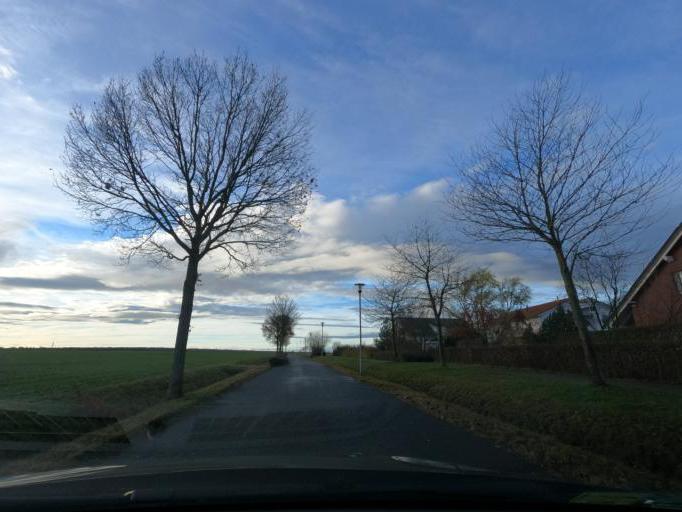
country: DE
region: Lower Saxony
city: Wolfenbuettel
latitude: 52.1508
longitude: 10.5220
